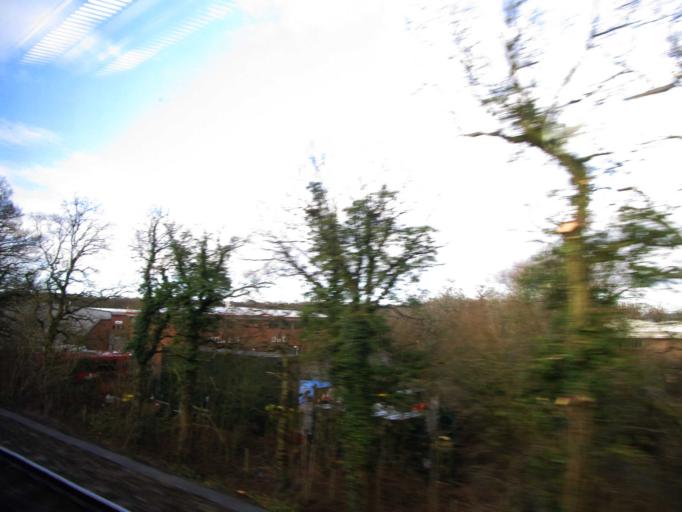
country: GB
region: England
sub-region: Hampshire
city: Basingstoke
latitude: 51.2945
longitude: -1.0631
